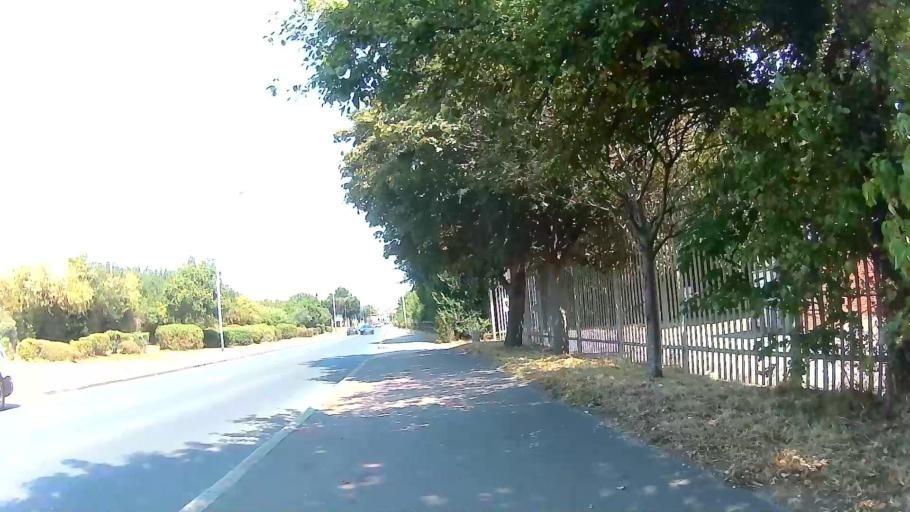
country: GB
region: England
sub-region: Greater London
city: Elm Park
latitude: 51.5235
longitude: 0.1916
